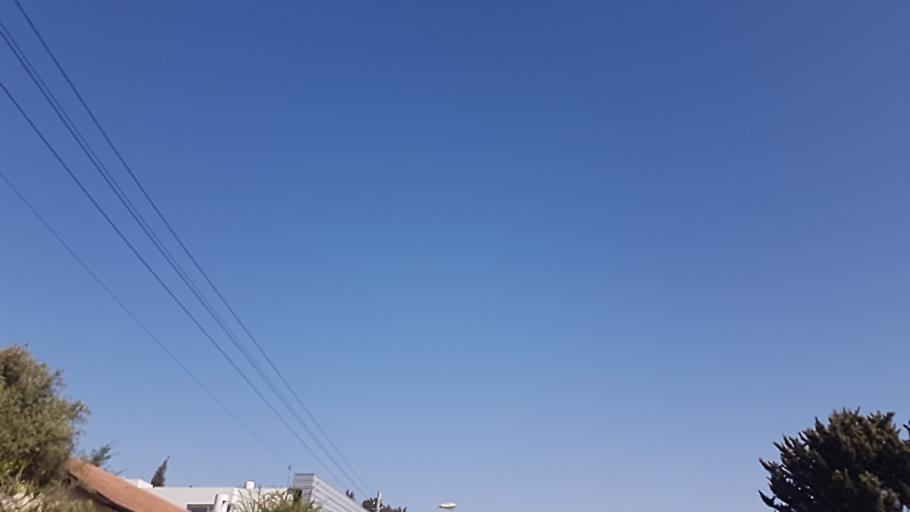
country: IL
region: Tel Aviv
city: Giv`atayim
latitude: 32.0590
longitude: 34.8236
